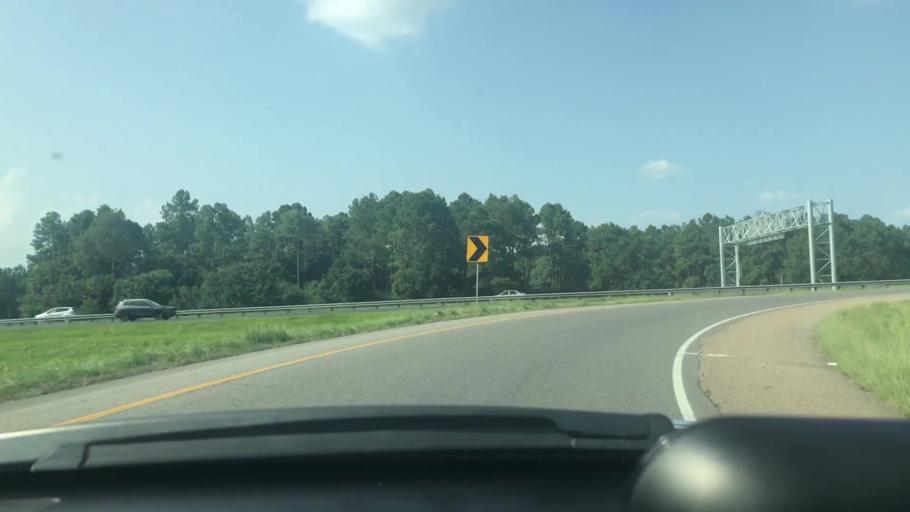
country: US
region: Louisiana
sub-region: Tangipahoa Parish
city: Hammond
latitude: 30.4782
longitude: -90.4901
